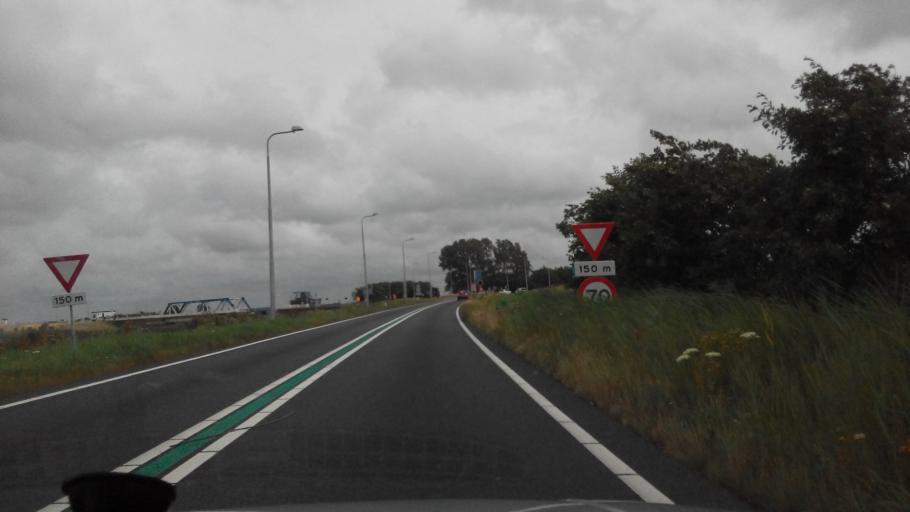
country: NL
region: North Holland
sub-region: Gemeente Schagen
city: Schagen
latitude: 52.8876
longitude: 4.8691
